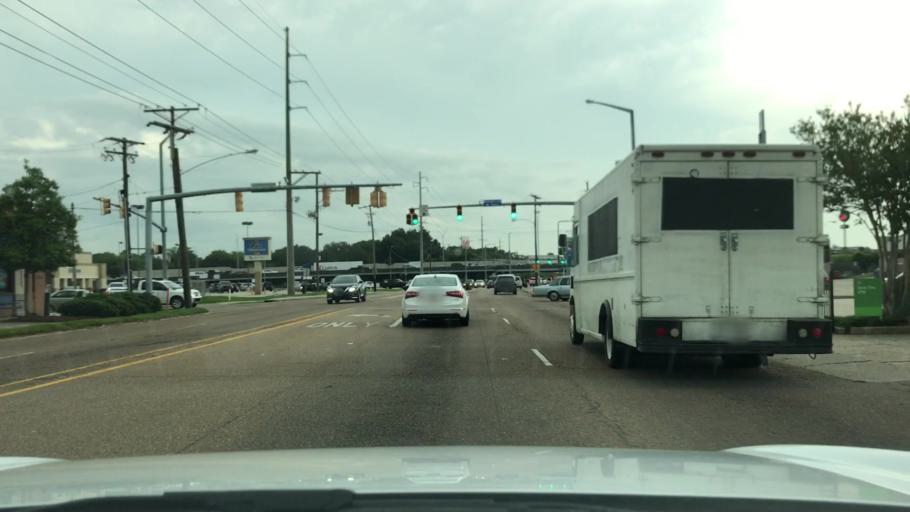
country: US
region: Louisiana
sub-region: East Baton Rouge Parish
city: Baton Rouge
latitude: 30.4205
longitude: -91.1407
